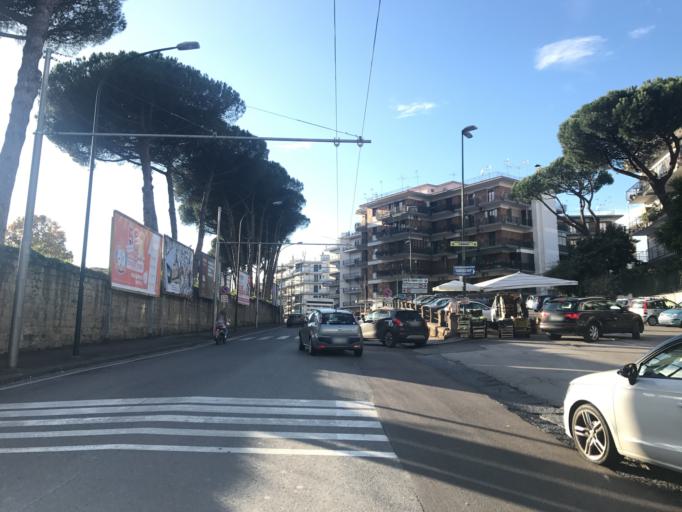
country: IT
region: Campania
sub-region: Provincia di Napoli
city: Napoli
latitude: 40.8687
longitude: 14.2255
